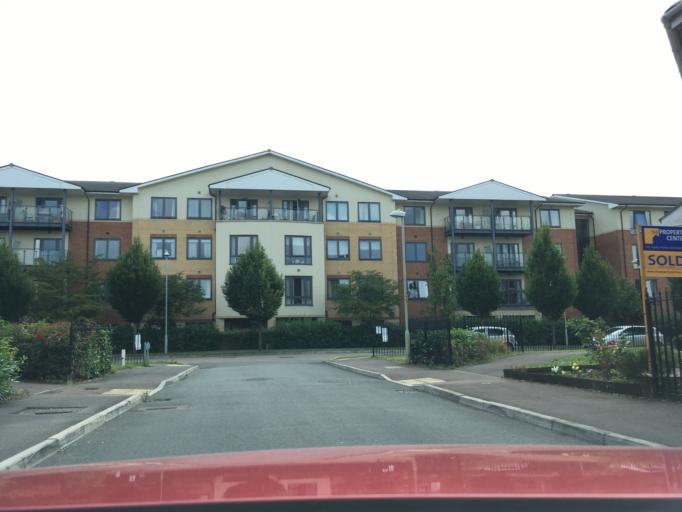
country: GB
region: England
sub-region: Gloucestershire
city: Gloucester
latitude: 51.8747
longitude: -2.2518
